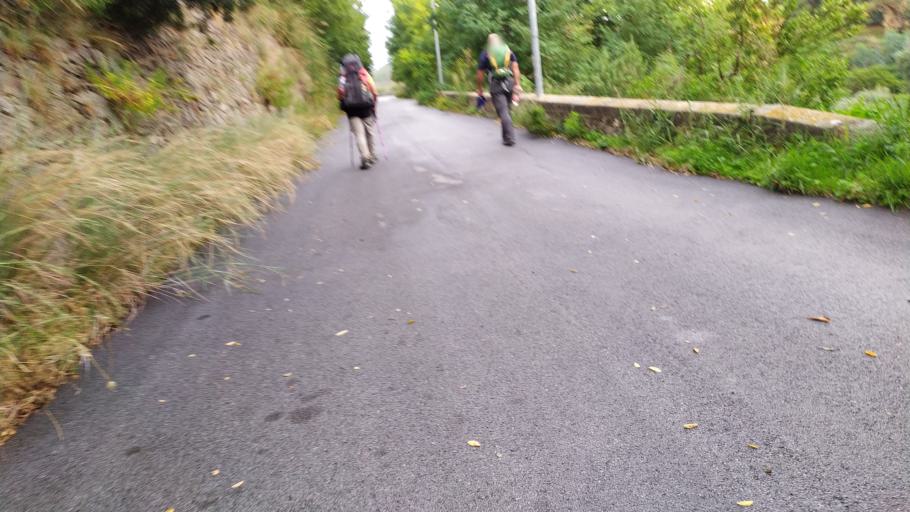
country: IT
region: Sicily
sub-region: Messina
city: Villafranca Tirrena
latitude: 38.2234
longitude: 15.4603
